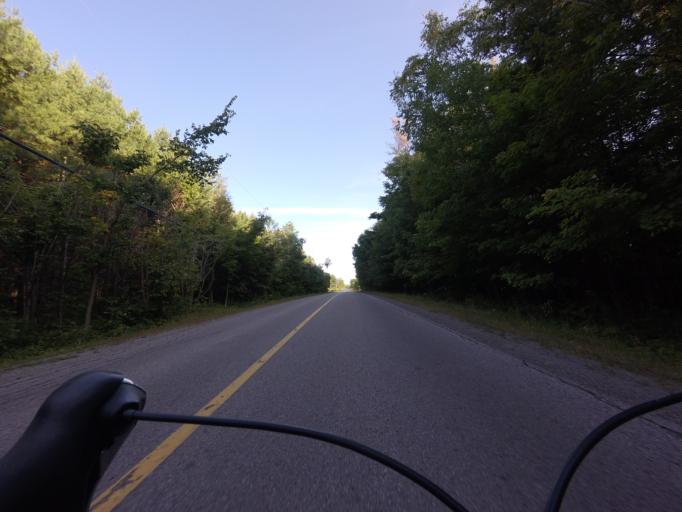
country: CA
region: Ontario
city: Bells Corners
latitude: 45.4214
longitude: -75.9716
